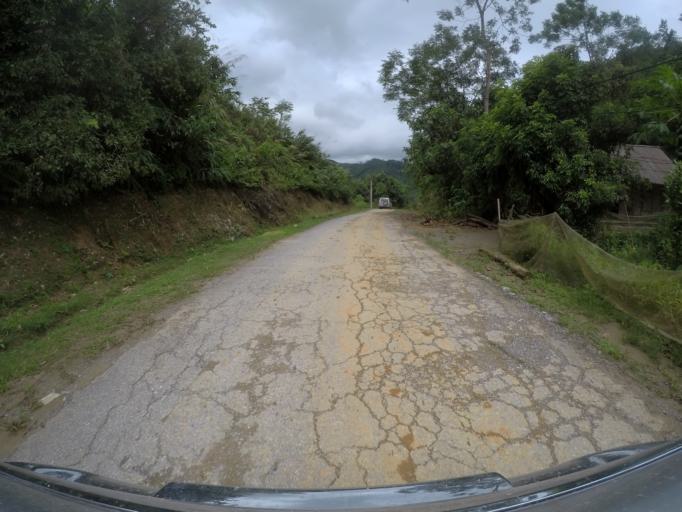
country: VN
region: Yen Bai
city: Co Phuc
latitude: 21.8176
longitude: 104.6240
